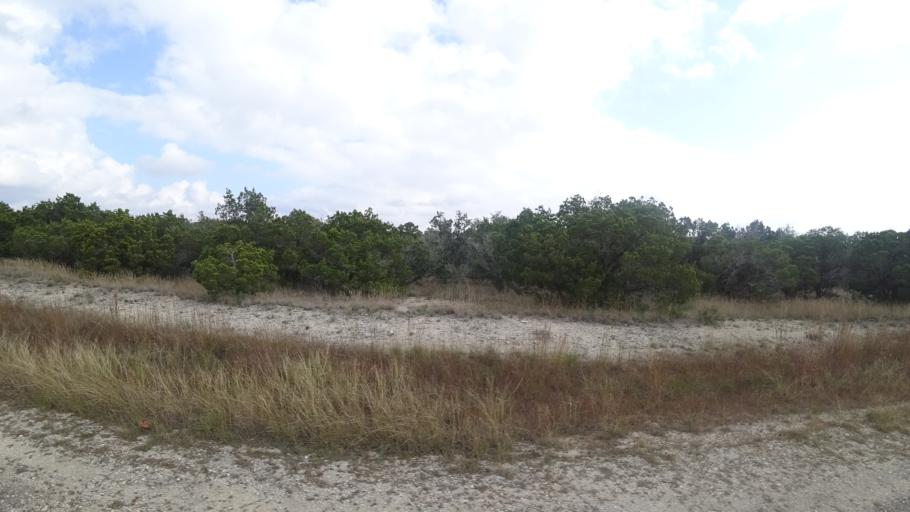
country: US
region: Texas
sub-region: Travis County
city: Barton Creek
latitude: 30.3025
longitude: -97.8910
